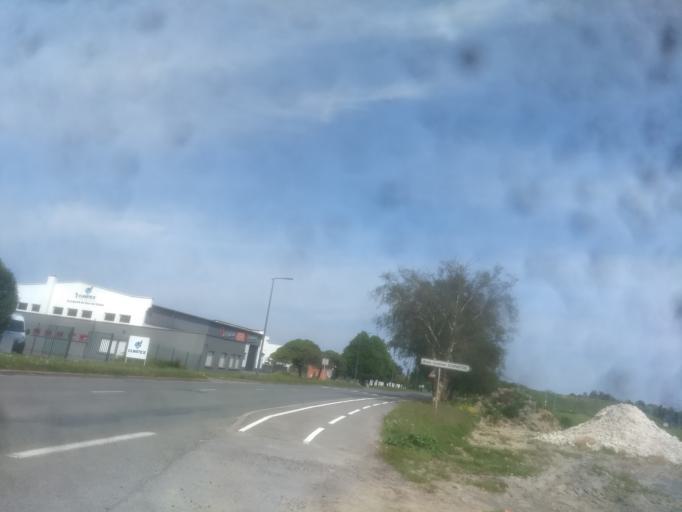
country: FR
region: Nord-Pas-de-Calais
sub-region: Departement du Pas-de-Calais
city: Tilloy-les-Mofflaines
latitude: 50.2834
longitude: 2.8132
